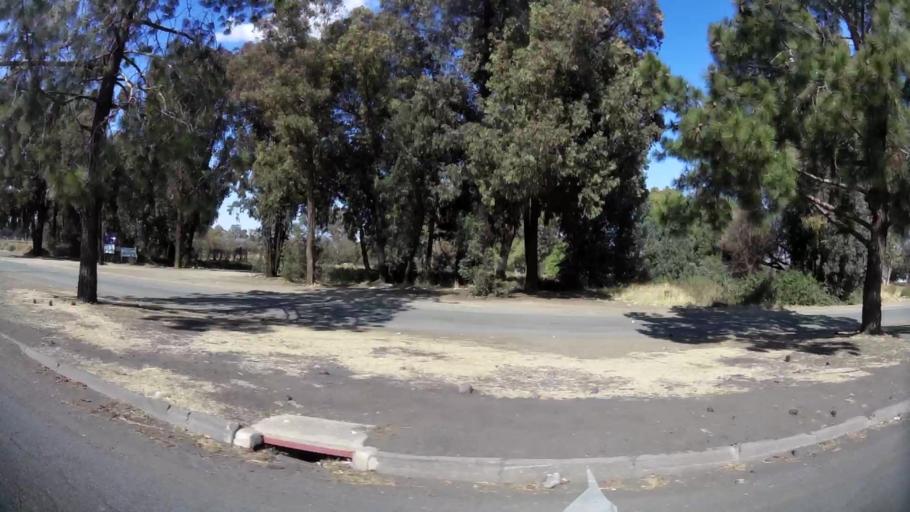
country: ZA
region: Orange Free State
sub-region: Mangaung Metropolitan Municipality
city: Bloemfontein
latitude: -29.1169
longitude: 26.2393
